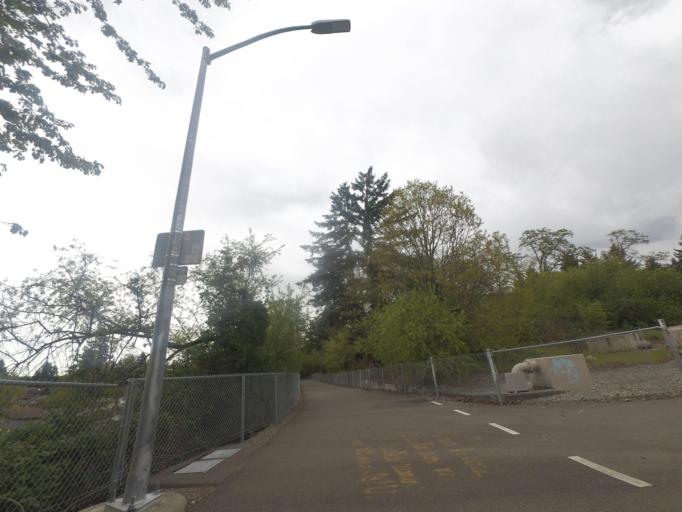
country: US
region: Washington
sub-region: Pierce County
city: Lakewood
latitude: 47.1860
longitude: -122.4804
